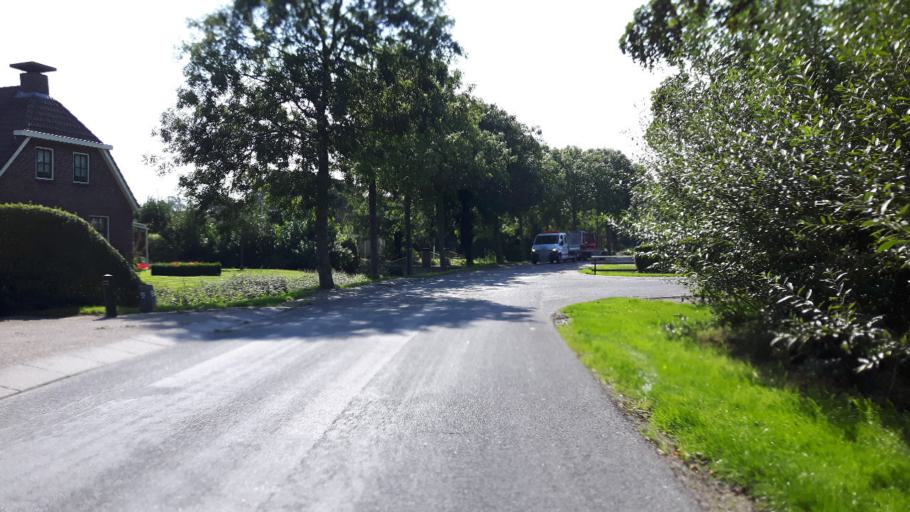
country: NL
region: Friesland
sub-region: Gemeente Ferwerderadiel
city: Hallum
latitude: 53.3097
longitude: 5.7849
